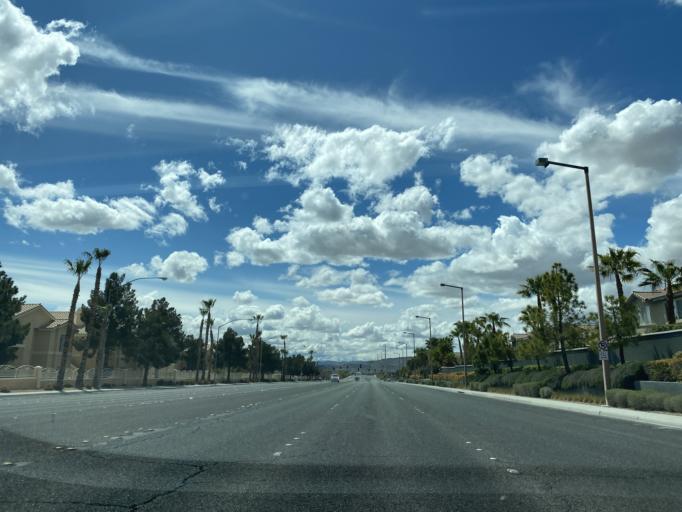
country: US
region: Nevada
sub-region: Clark County
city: Summerlin South
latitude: 36.1253
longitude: -115.3152
